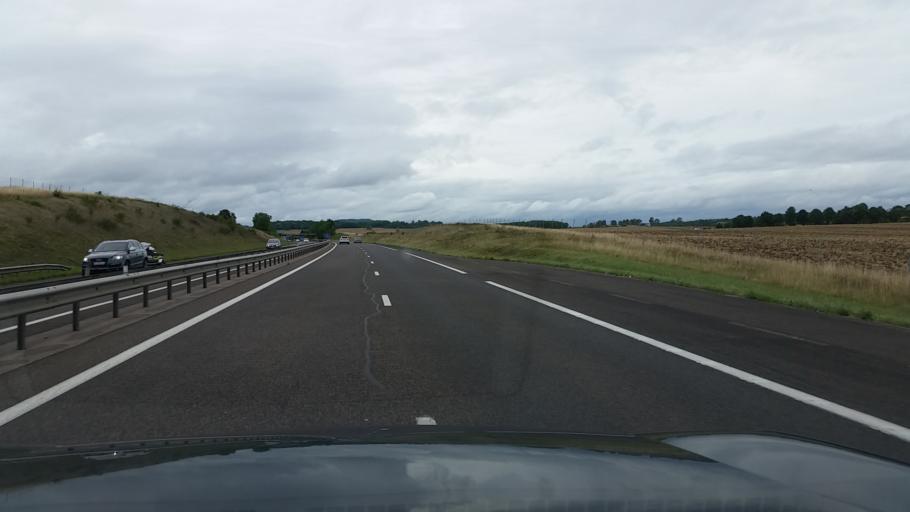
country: FR
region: Lorraine
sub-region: Departement de Meurthe-et-Moselle
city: Blenod-les-Toul
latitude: 48.6163
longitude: 5.8868
